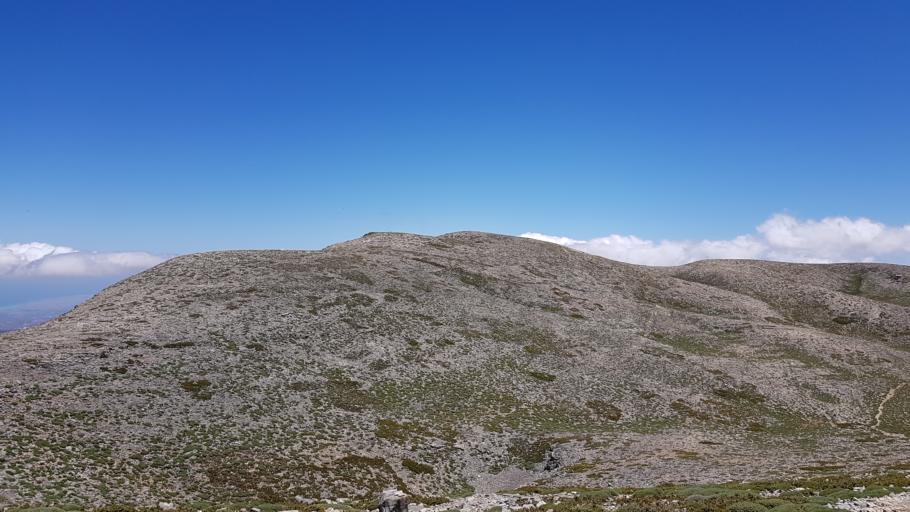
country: GR
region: Crete
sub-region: Nomos Rethymnis
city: Zoniana
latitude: 35.2234
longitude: 24.7897
